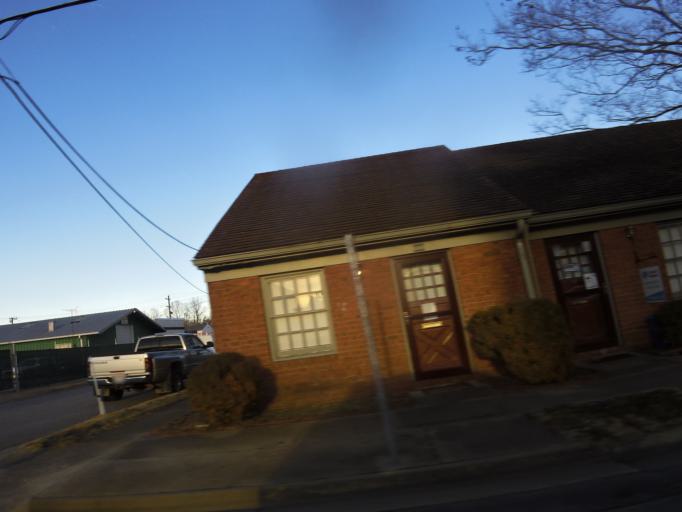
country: US
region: Virginia
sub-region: City of Franklin
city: Franklin
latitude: 36.6788
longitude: -76.9225
